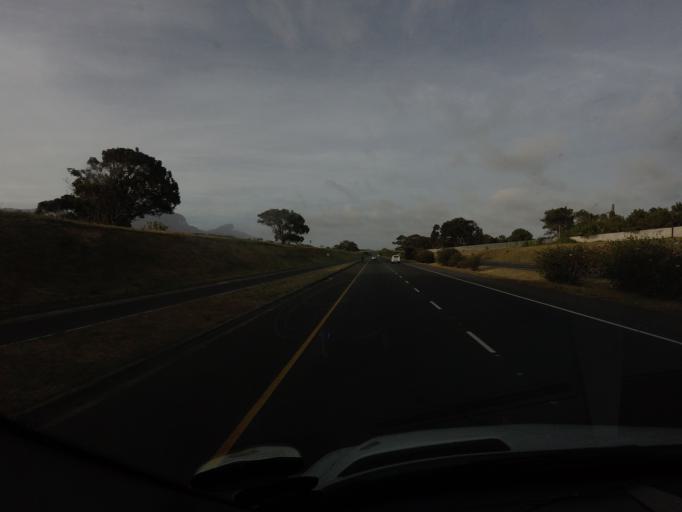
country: ZA
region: Western Cape
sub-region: City of Cape Town
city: Bergvliet
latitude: -34.0306
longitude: 18.4456
